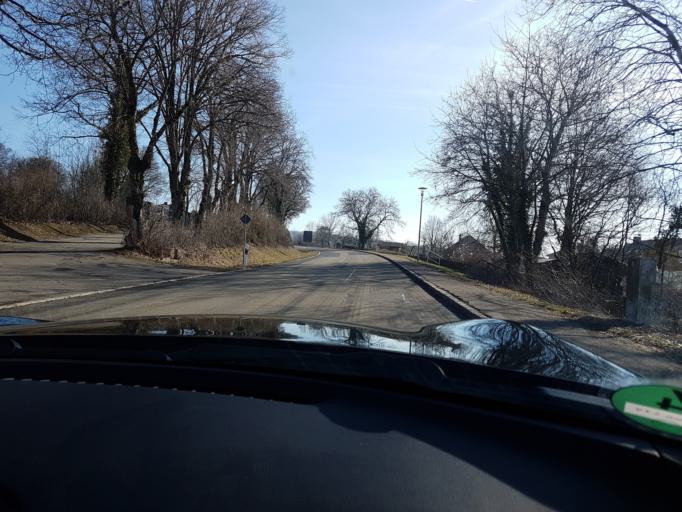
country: DE
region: Baden-Wuerttemberg
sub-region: Regierungsbezirk Stuttgart
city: Langenburg
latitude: 49.2515
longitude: 9.8578
